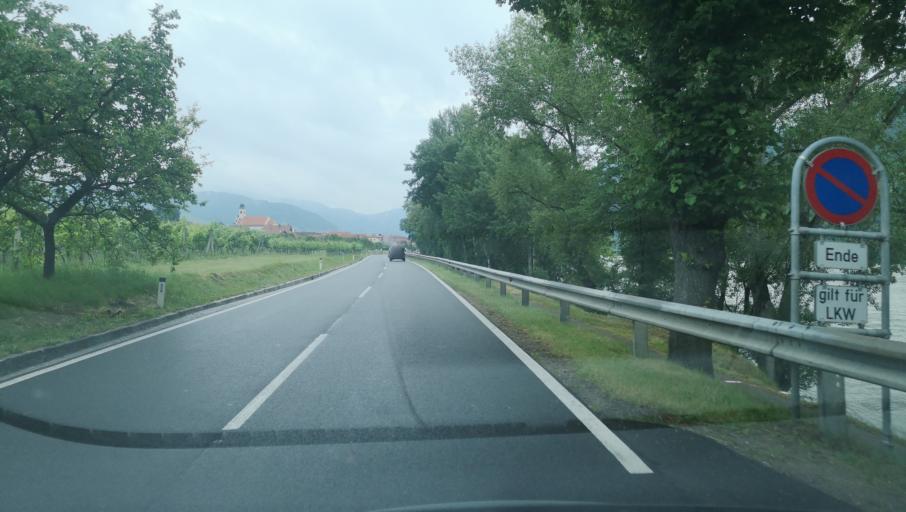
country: AT
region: Lower Austria
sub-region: Politischer Bezirk Krems
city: Spitz
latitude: 48.3769
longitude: 15.4507
